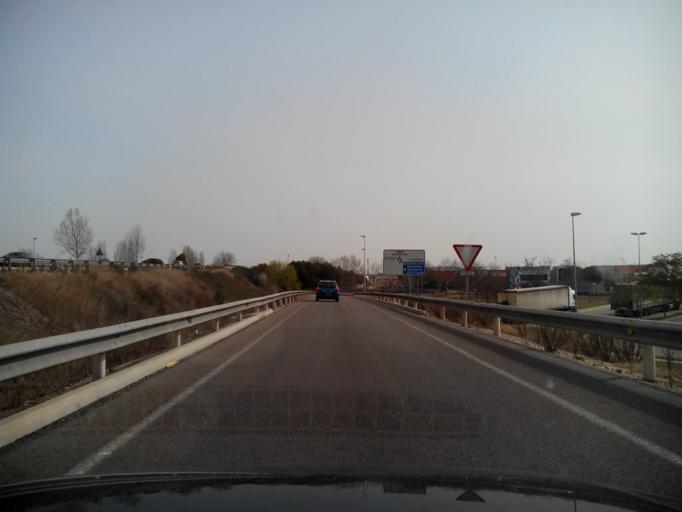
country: ES
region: Catalonia
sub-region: Provincia de Barcelona
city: Vilafranca del Penedes
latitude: 41.3343
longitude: 1.6802
